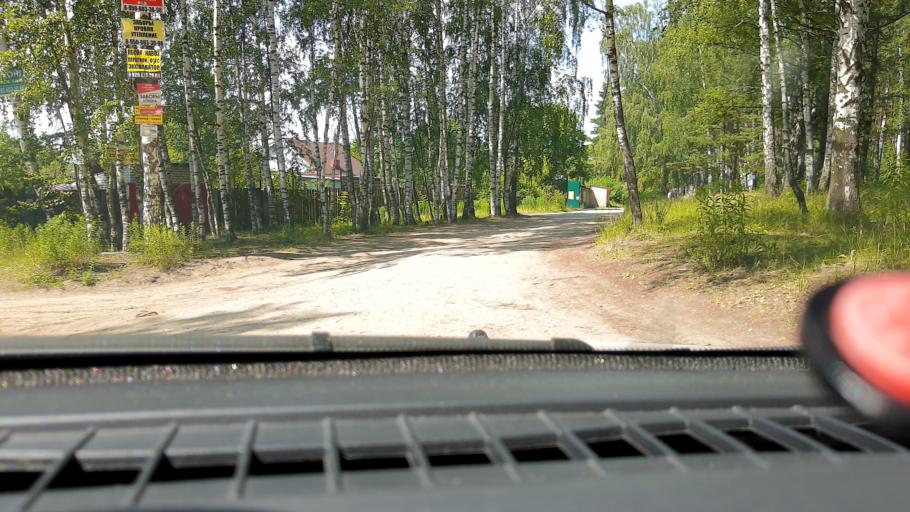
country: RU
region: Nizjnij Novgorod
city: Neklyudovo
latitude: 56.4503
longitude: 43.9967
